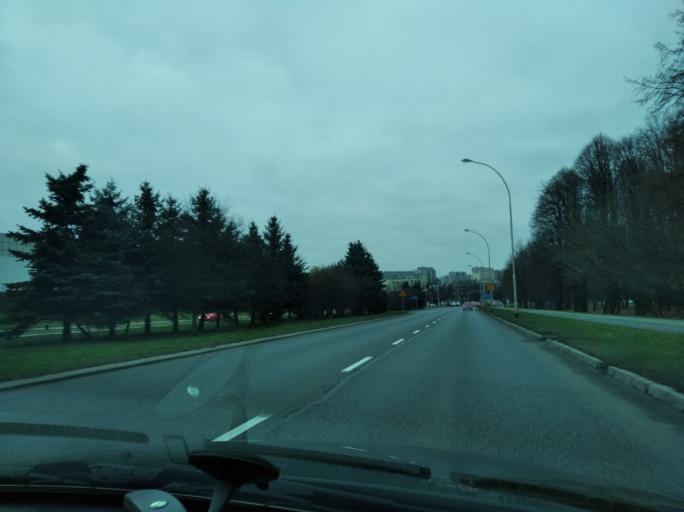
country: PL
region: Subcarpathian Voivodeship
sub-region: Rzeszow
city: Rzeszow
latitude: 50.0383
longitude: 21.9773
